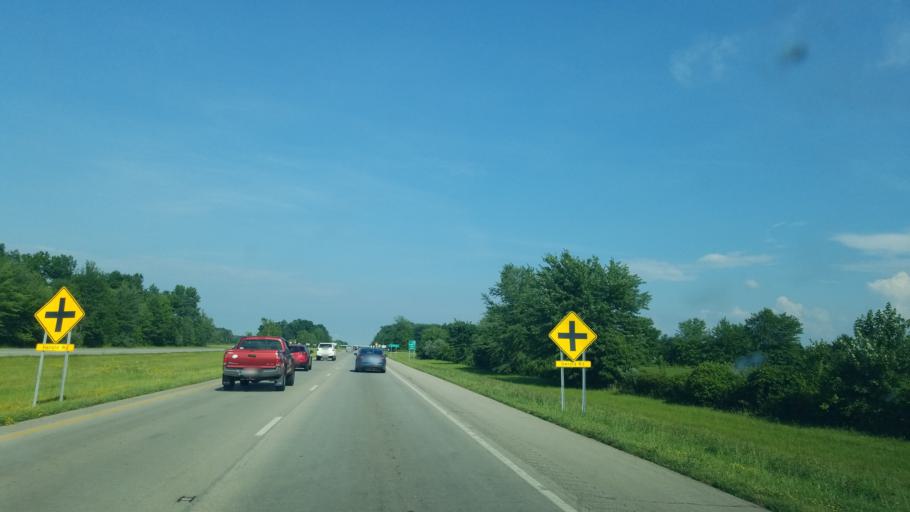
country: US
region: Ohio
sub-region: Clermont County
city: Batavia
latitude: 39.0803
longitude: -84.1389
